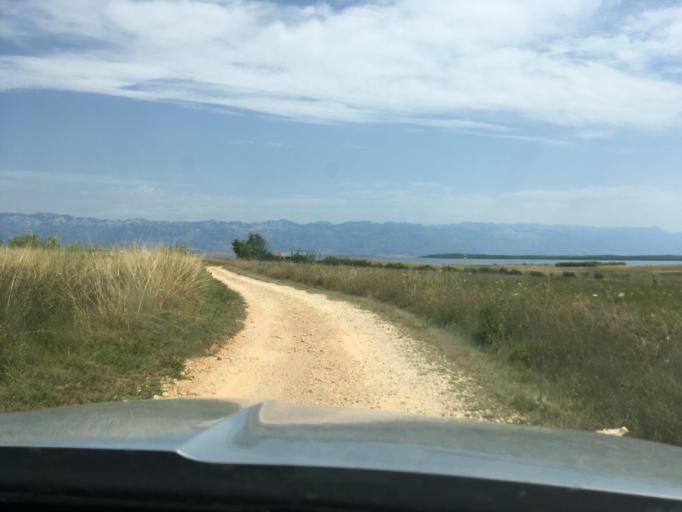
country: HR
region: Zadarska
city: Privlaka
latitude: 44.2639
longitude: 15.1472
